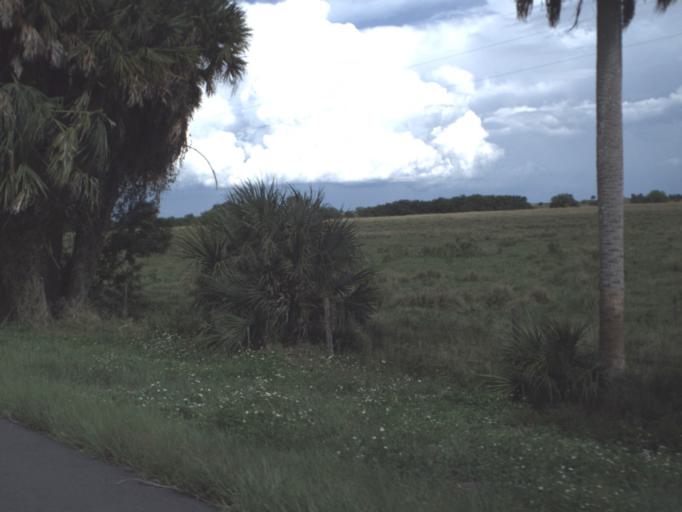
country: US
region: Florida
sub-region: Glades County
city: Buckhead Ridge
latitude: 27.1060
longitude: -80.9455
